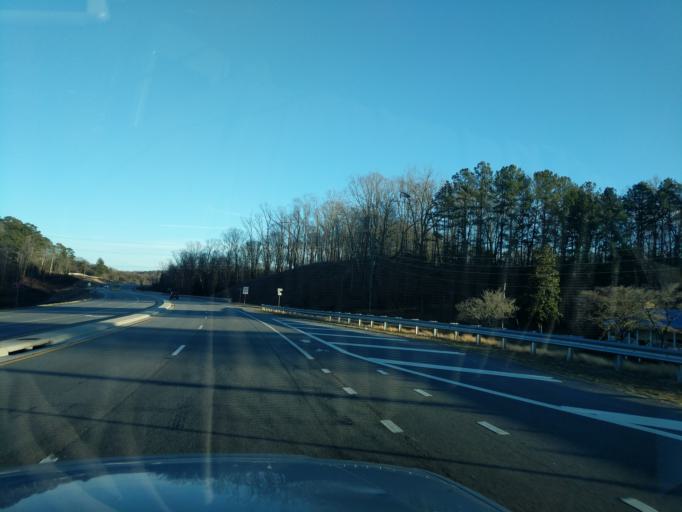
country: US
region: Georgia
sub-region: Stephens County
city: Toccoa
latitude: 34.5355
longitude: -83.2624
